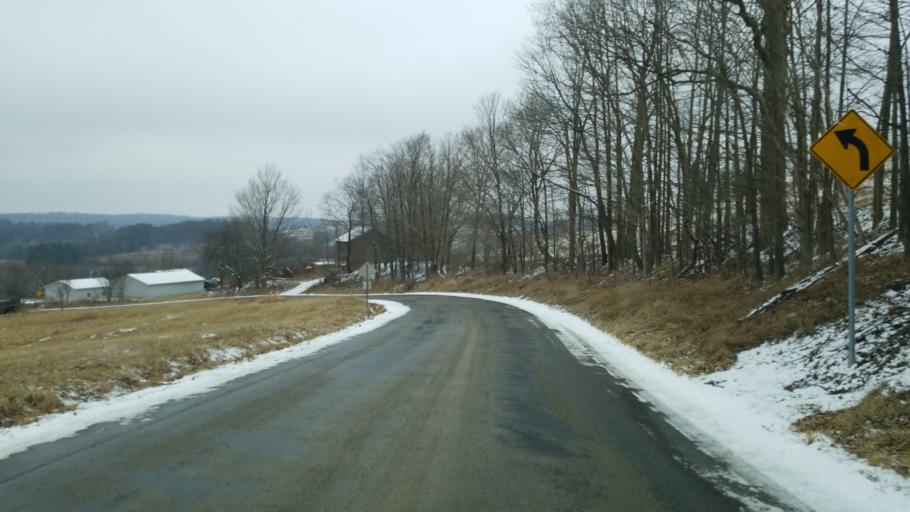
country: US
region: Pennsylvania
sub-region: Jefferson County
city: Reynoldsville
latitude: 41.0871
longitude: -78.8530
